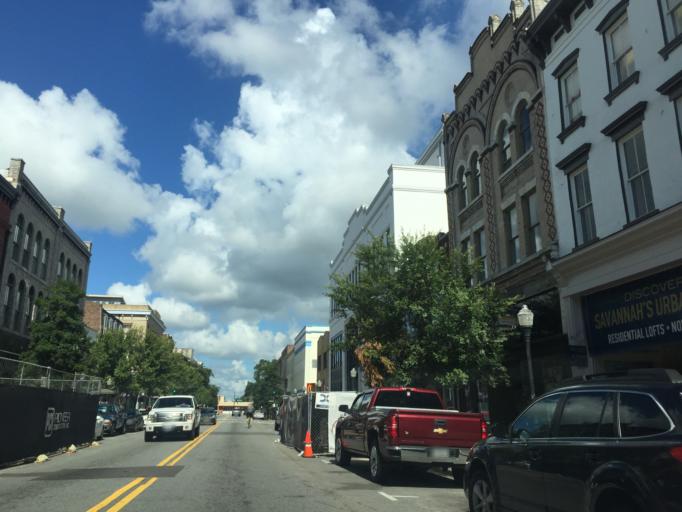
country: US
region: Georgia
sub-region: Chatham County
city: Savannah
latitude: 32.0796
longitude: -81.0945
